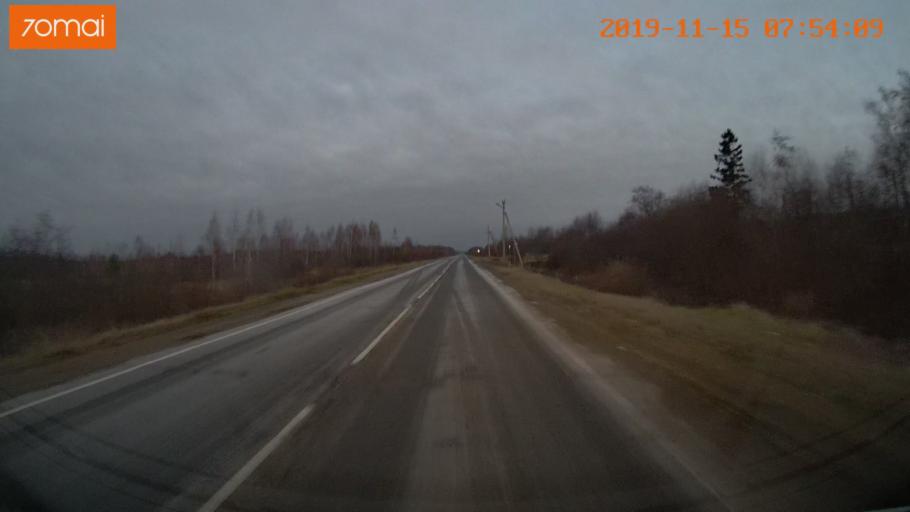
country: RU
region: Vologda
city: Cherepovets
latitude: 58.8958
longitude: 38.1791
